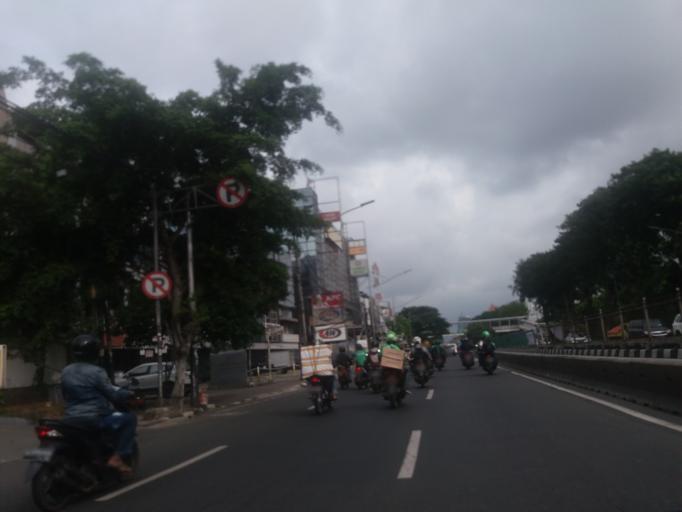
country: ID
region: Jakarta Raya
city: Jakarta
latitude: -6.1608
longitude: 106.8379
